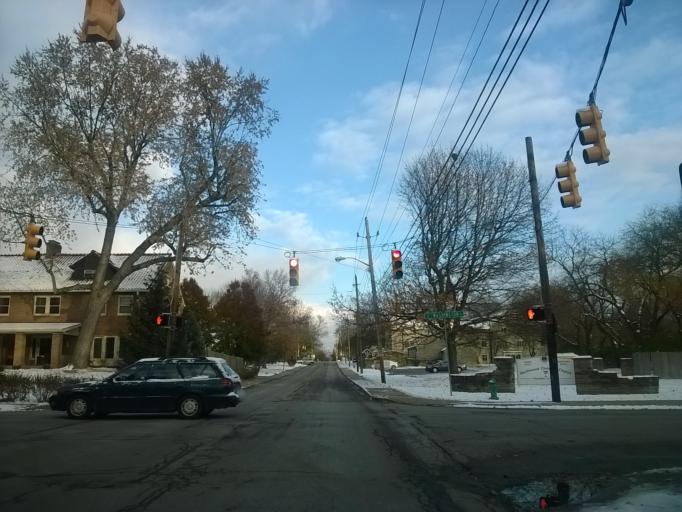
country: US
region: Indiana
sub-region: Marion County
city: Broad Ripple
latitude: 39.8395
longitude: -86.1524
